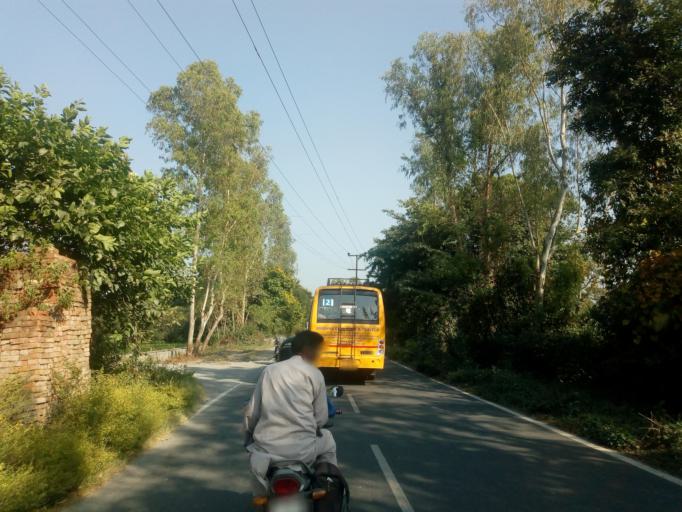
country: IN
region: Uttarakhand
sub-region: Dehradun
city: Harbatpur
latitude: 30.4416
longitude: 77.6964
